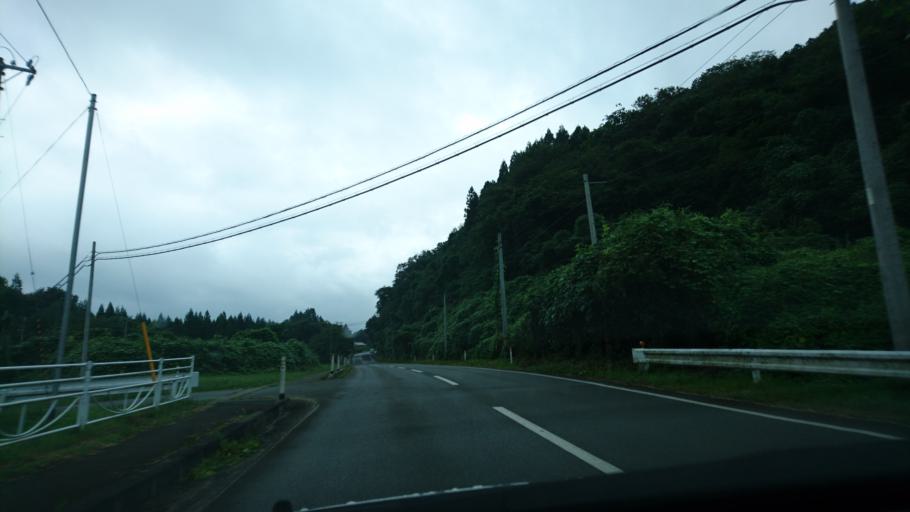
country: JP
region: Iwate
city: Ichinoseki
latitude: 38.9166
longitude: 141.0835
